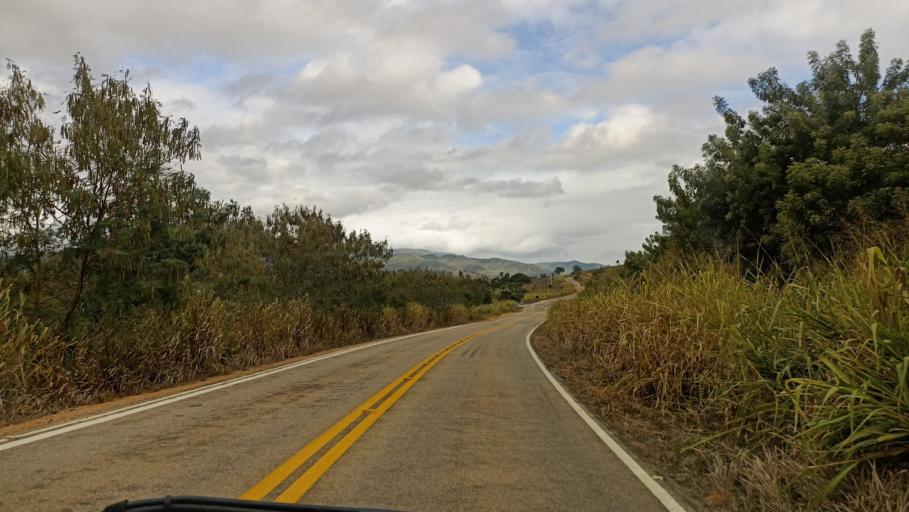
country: BR
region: Minas Gerais
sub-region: Joaima
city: Joaima
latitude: -16.6957
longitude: -40.9558
